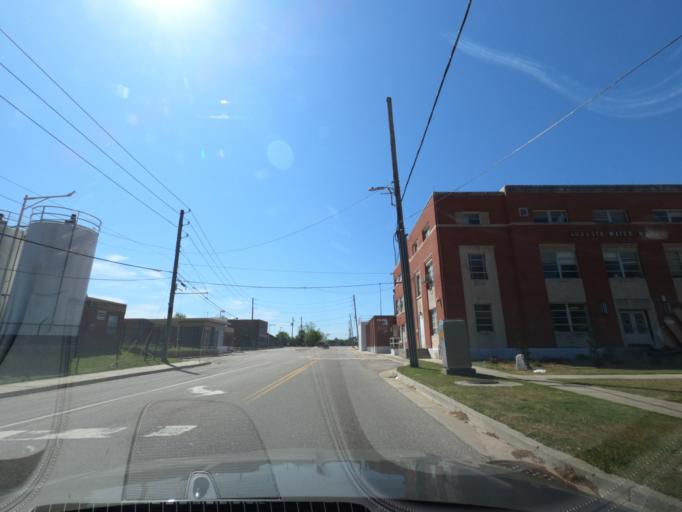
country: US
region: Georgia
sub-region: Richmond County
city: Augusta
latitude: 33.4709
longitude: -82.0314
